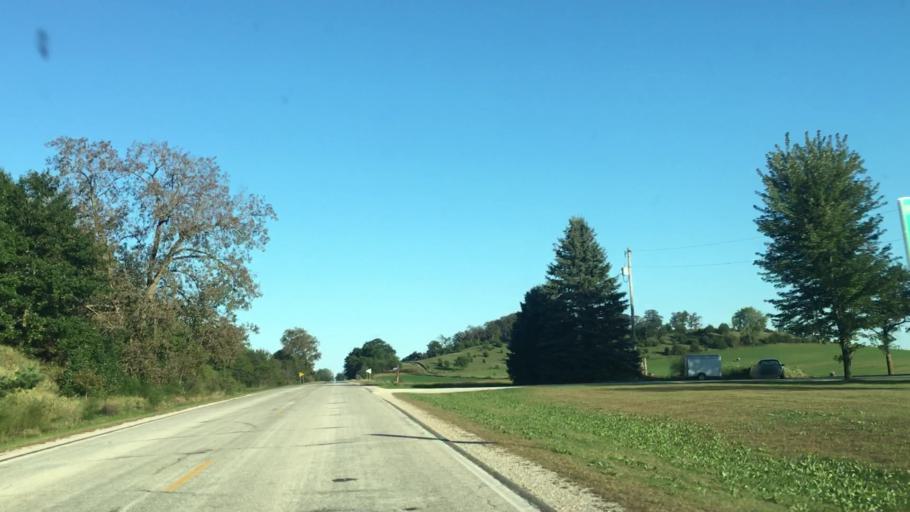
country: US
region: Minnesota
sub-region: Fillmore County
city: Chatfield
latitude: 43.8416
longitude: -92.0863
